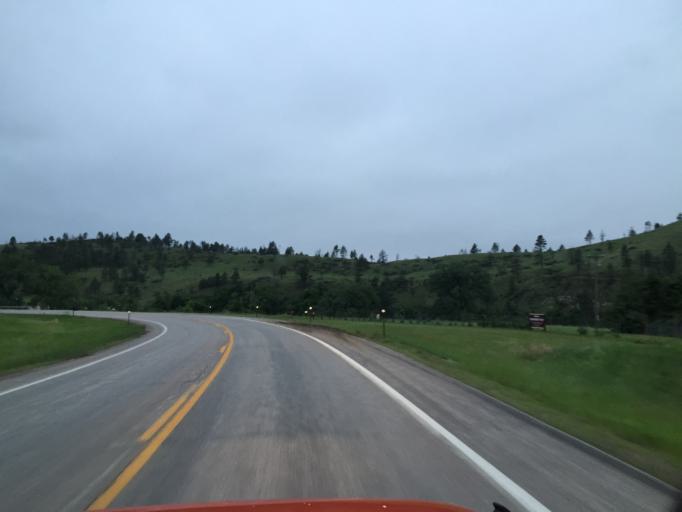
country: US
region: South Dakota
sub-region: Pennington County
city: Colonial Pine Hills
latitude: 43.8301
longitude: -103.2376
